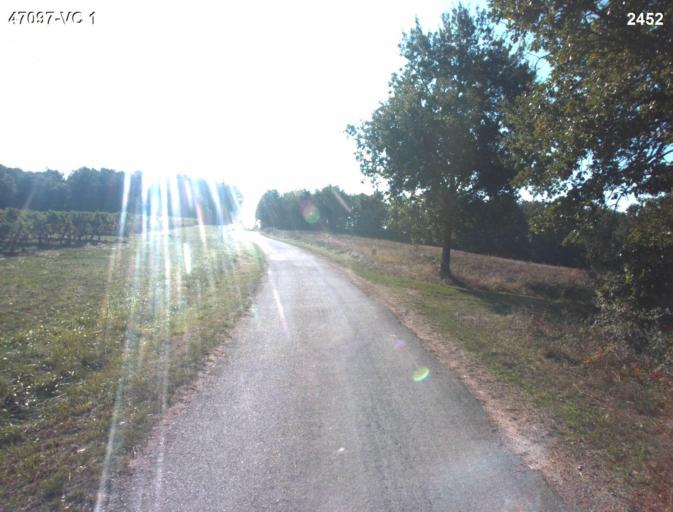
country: FR
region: Aquitaine
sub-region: Departement du Lot-et-Garonne
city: Vianne
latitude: 44.2043
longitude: 0.3586
